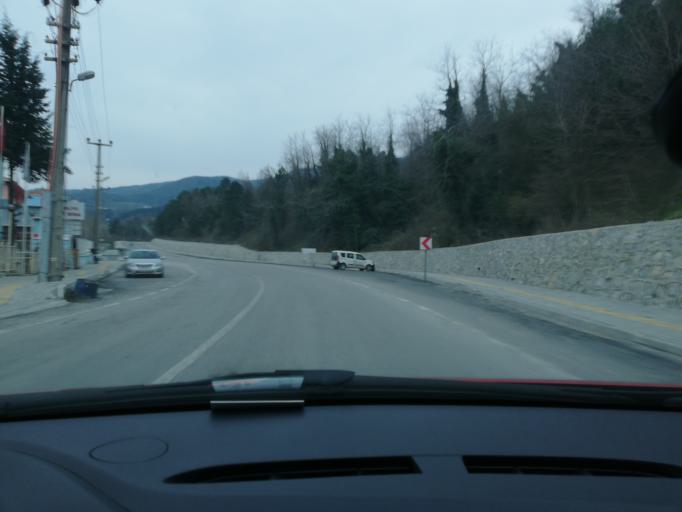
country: TR
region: Kastamonu
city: Inebolu
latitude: 41.9752
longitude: 33.7728
